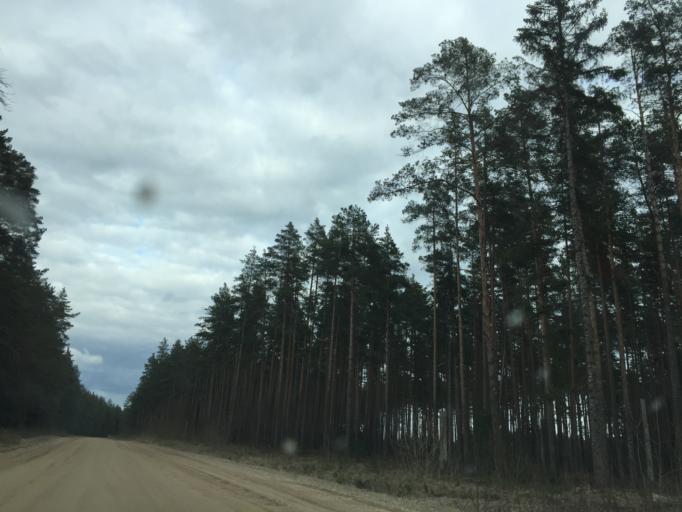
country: LV
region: Lielvarde
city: Lielvarde
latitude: 56.5373
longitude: 24.8283
